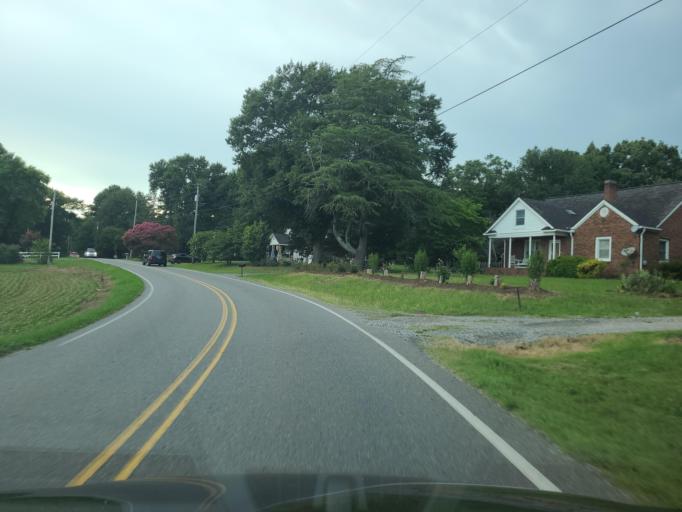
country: US
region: North Carolina
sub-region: Gaston County
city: Dallas
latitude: 35.3024
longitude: -81.1644
